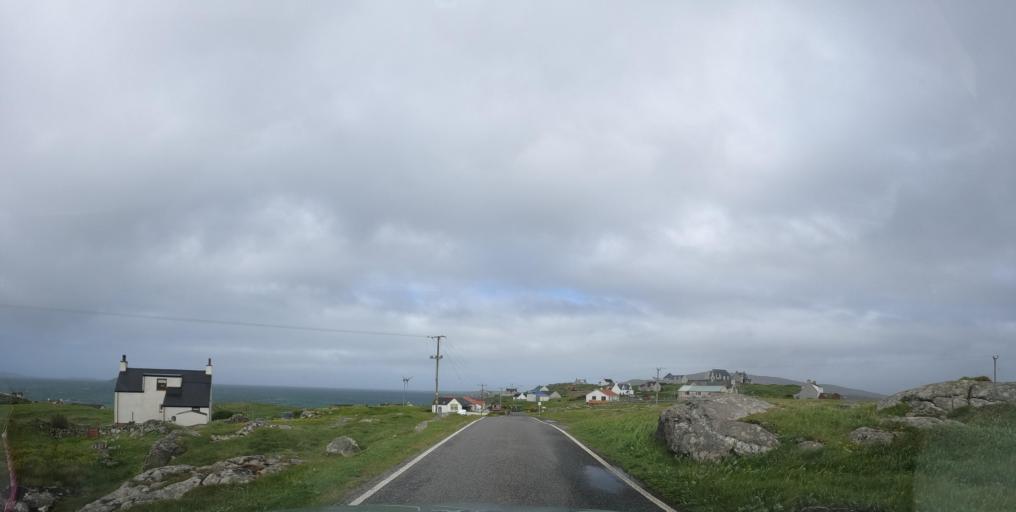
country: GB
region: Scotland
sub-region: Eilean Siar
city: Isle of South Uist
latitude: 57.0837
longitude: -7.3042
